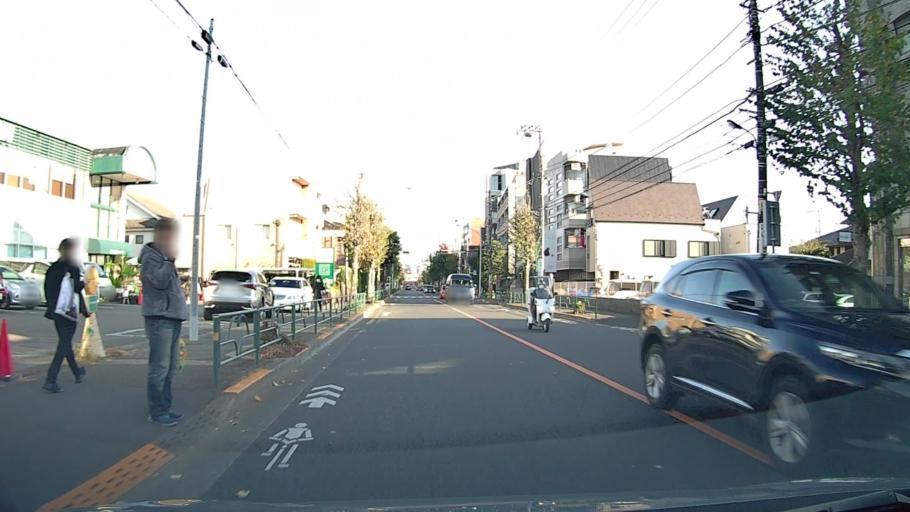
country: JP
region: Tokyo
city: Musashino
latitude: 35.7045
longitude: 139.5718
